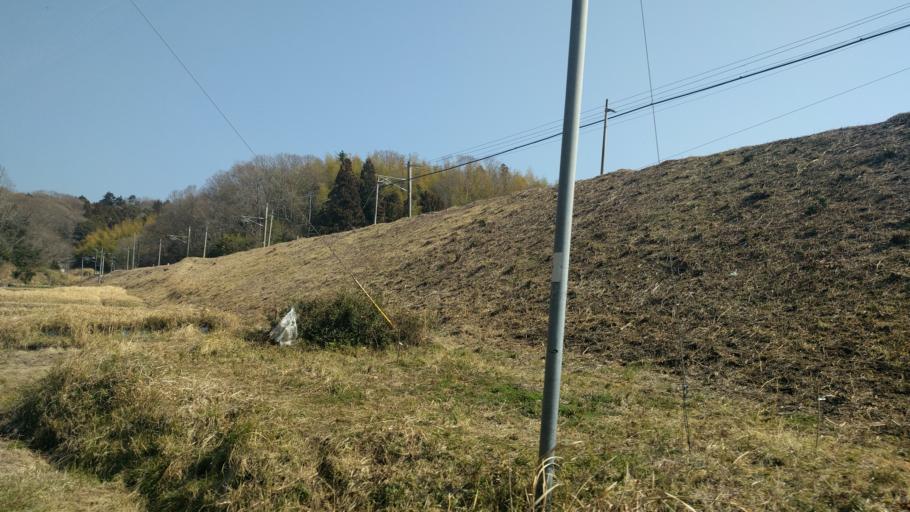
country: JP
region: Fukushima
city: Iwaki
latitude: 37.1565
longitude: 140.9982
